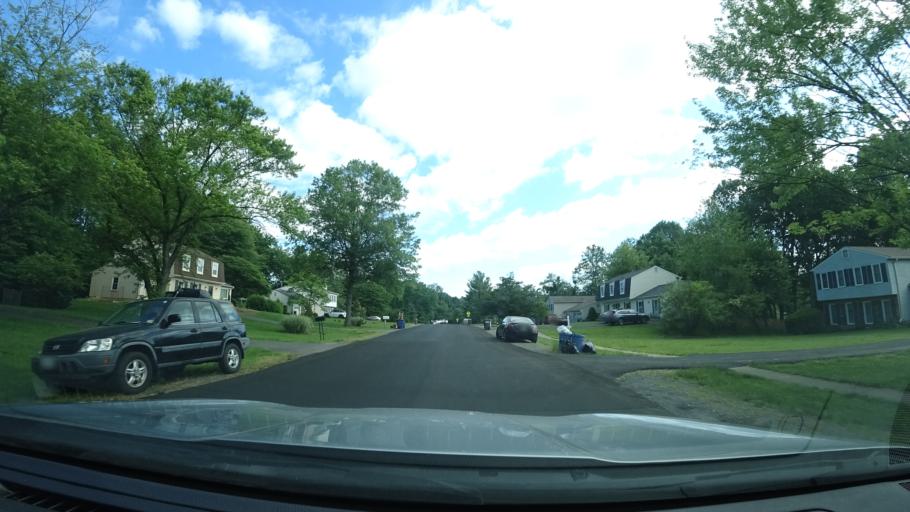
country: US
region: Virginia
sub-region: Fairfax County
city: Oak Hill
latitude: 38.9385
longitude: -77.3751
